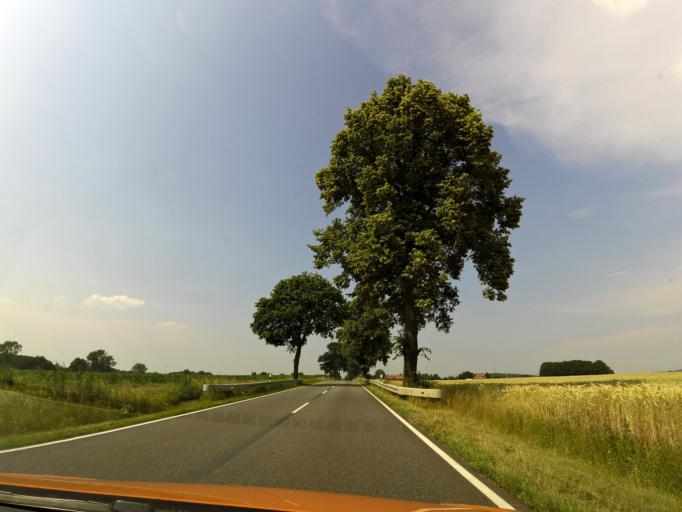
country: DE
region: Mecklenburg-Vorpommern
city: Krakow am See
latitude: 53.7220
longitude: 12.2777
